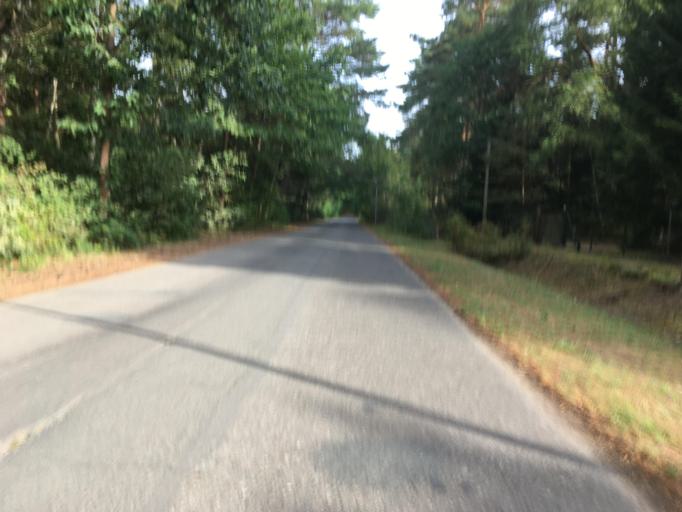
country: DE
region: Brandenburg
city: Marienwerder
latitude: 52.9220
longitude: 13.5214
